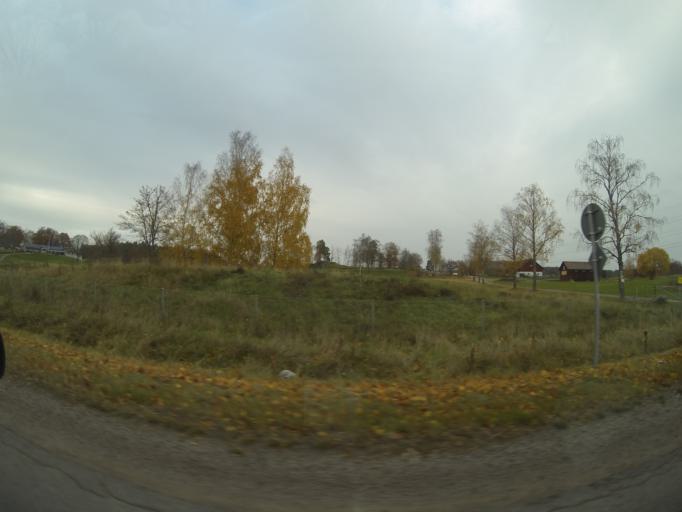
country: SE
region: Vaestmanland
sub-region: Vasteras
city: Vasteras
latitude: 59.6268
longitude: 16.5047
